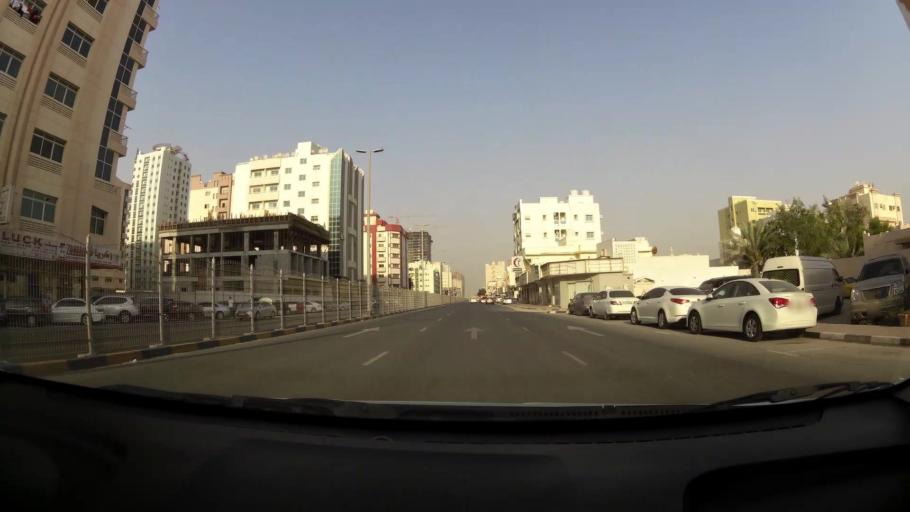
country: AE
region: Ajman
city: Ajman
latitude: 25.3873
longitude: 55.4482
